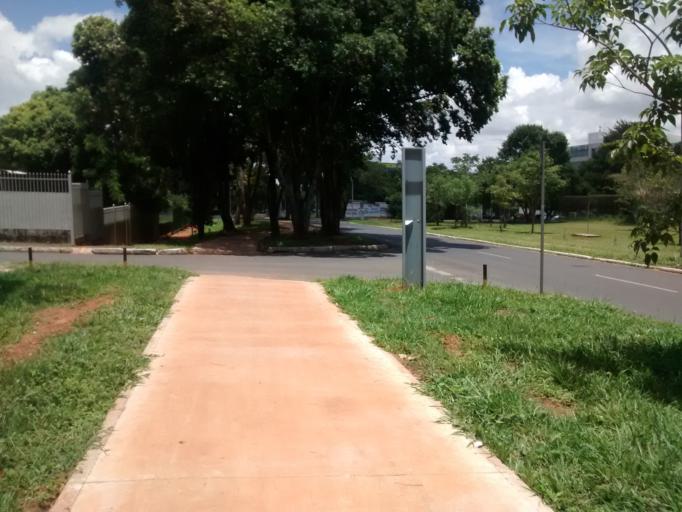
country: BR
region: Federal District
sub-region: Brasilia
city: Brasilia
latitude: -15.8106
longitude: -47.9082
